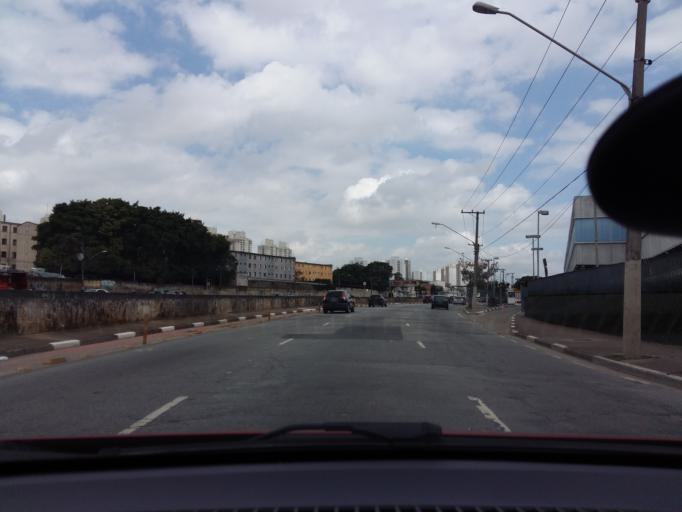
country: BR
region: Sao Paulo
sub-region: Sao Caetano Do Sul
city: Sao Caetano do Sul
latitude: -23.5931
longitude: -46.5851
